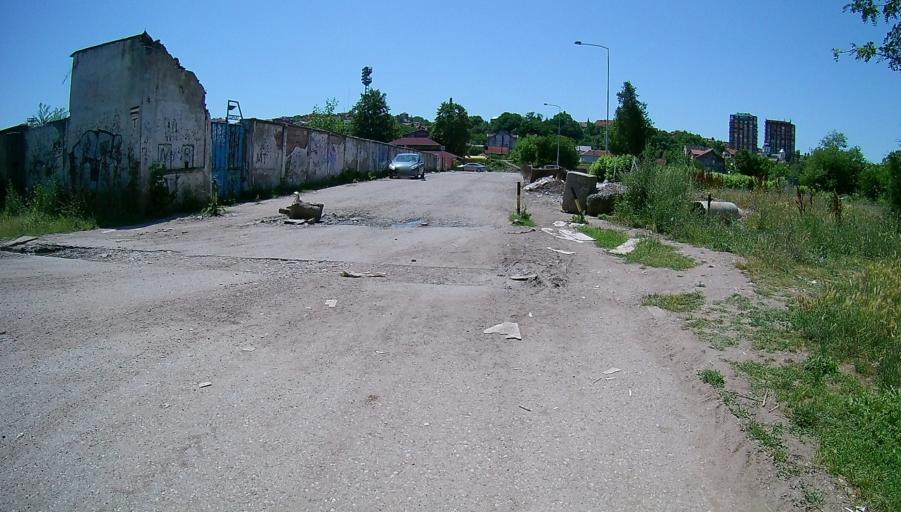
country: RS
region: Central Serbia
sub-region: Nisavski Okrug
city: Nis
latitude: 43.3136
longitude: 21.9046
